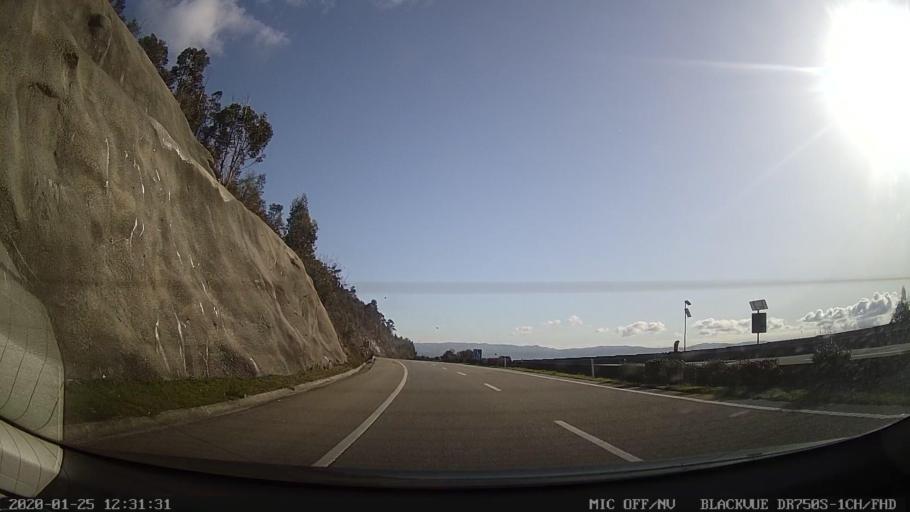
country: PT
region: Aveiro
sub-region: Sever do Vouga
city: Sever do Vouga
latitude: 40.6654
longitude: -8.3246
